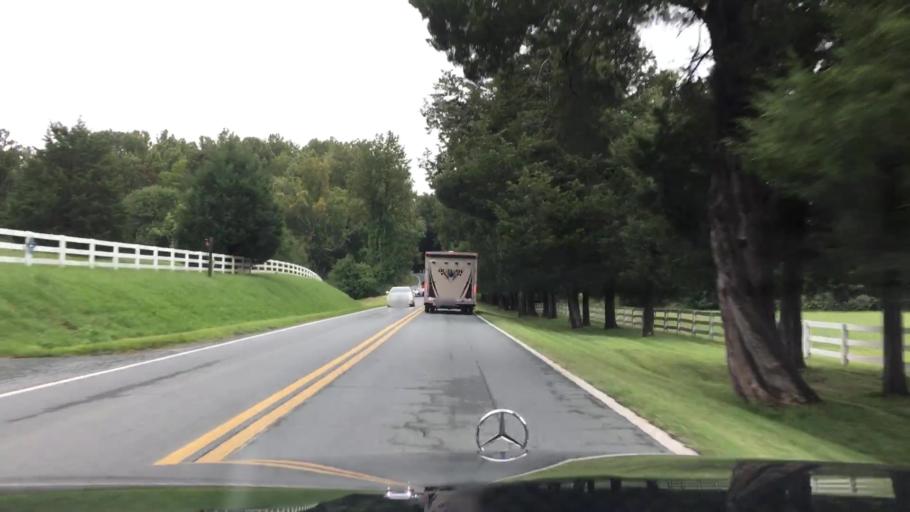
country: US
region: Virginia
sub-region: Orange County
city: Gordonsville
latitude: 38.0670
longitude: -78.3044
